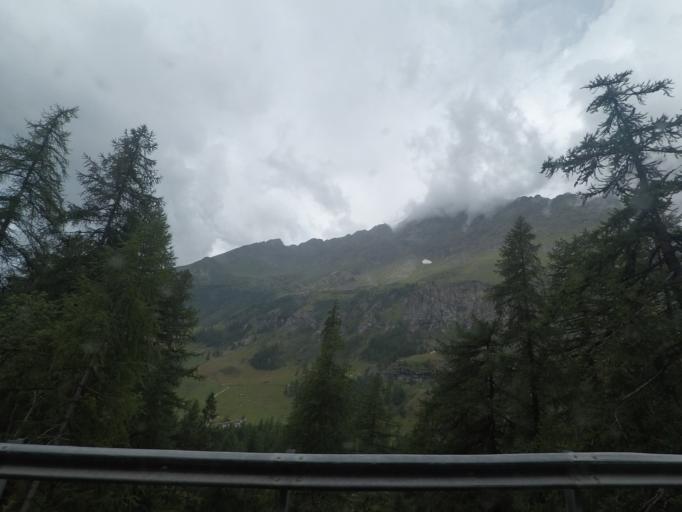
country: IT
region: Aosta Valley
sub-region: Valle d'Aosta
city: Paquier
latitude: 45.9140
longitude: 7.6174
